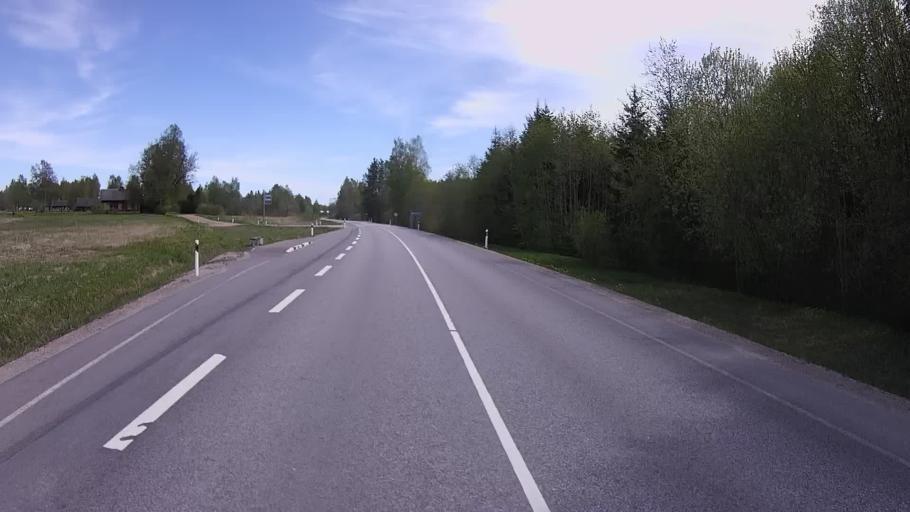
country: EE
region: Valgamaa
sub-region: Valga linn
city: Valga
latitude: 57.7126
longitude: 26.2169
